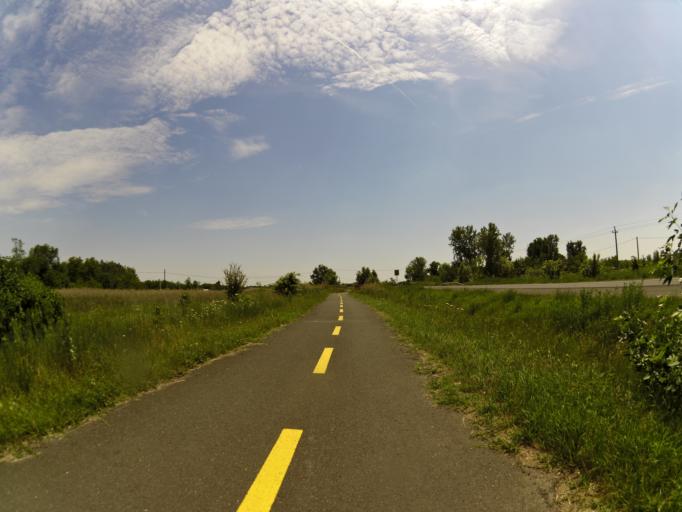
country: HU
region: Csongrad
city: Balastya
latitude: 46.4363
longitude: 20.0069
